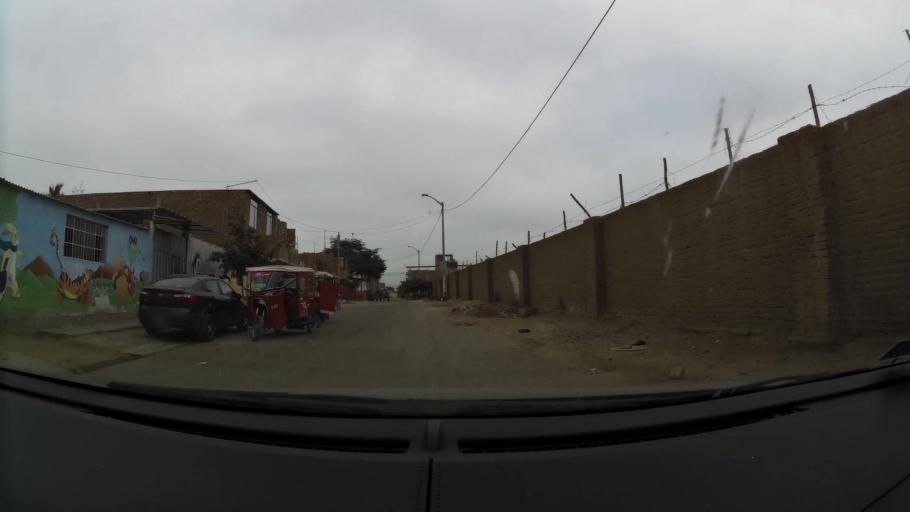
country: PE
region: La Libertad
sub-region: Provincia de Trujillo
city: La Esperanza
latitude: -8.0810
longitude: -79.0516
